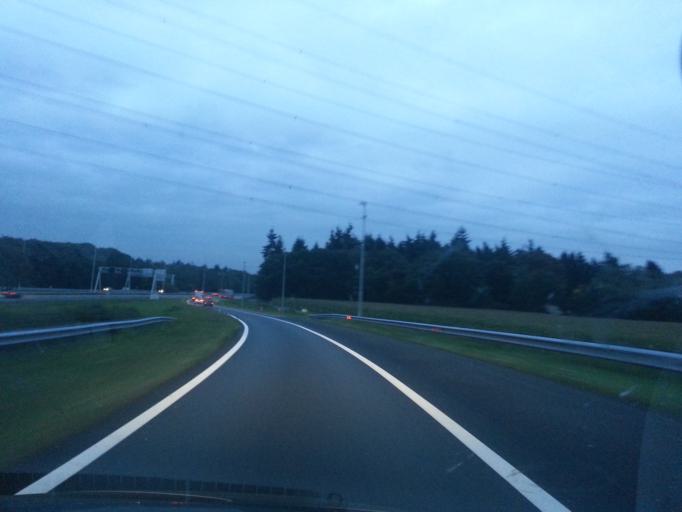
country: NL
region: North Brabant
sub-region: Gemeente Tilburg
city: Tilburg
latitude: 51.5507
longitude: 5.1325
